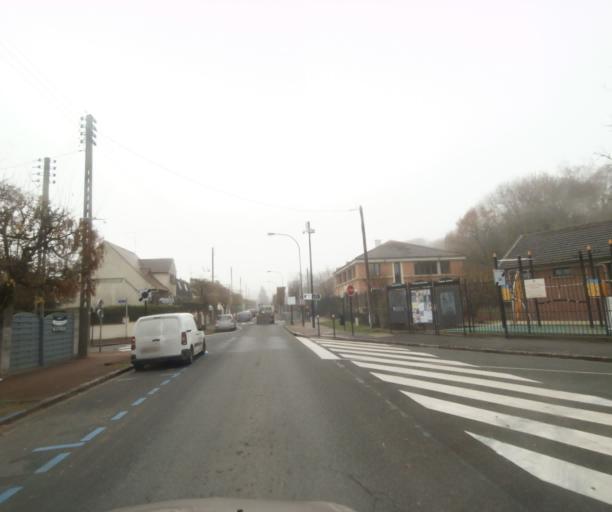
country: FR
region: Ile-de-France
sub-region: Departement de Seine-Saint-Denis
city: Vaujours
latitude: 48.9385
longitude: 2.5688
